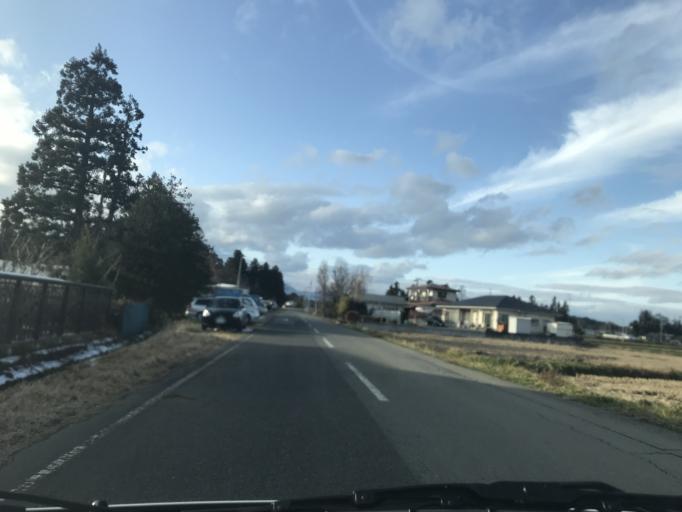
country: JP
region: Iwate
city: Mizusawa
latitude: 39.1887
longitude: 141.0956
